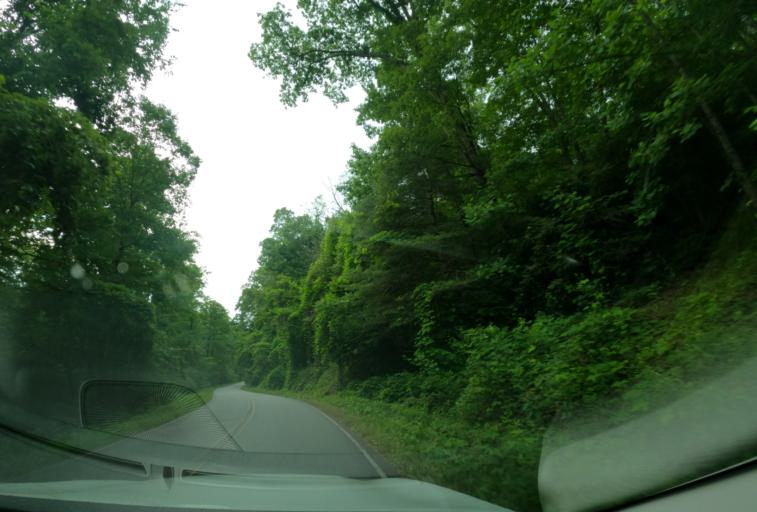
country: US
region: North Carolina
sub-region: Transylvania County
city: Brevard
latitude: 35.2852
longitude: -82.7960
